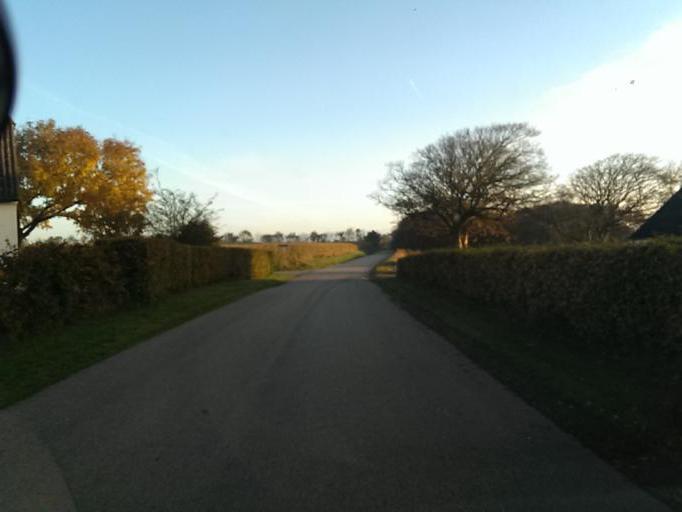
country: DK
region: South Denmark
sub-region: Esbjerg Kommune
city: Tjaereborg
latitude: 55.4810
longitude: 8.6344
